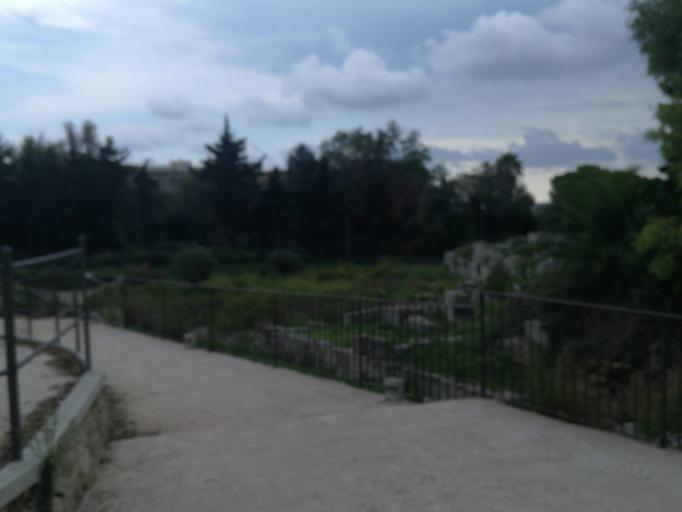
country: IT
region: Sicily
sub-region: Provincia di Siracusa
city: Siracusa
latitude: 37.0738
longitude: 15.2793
